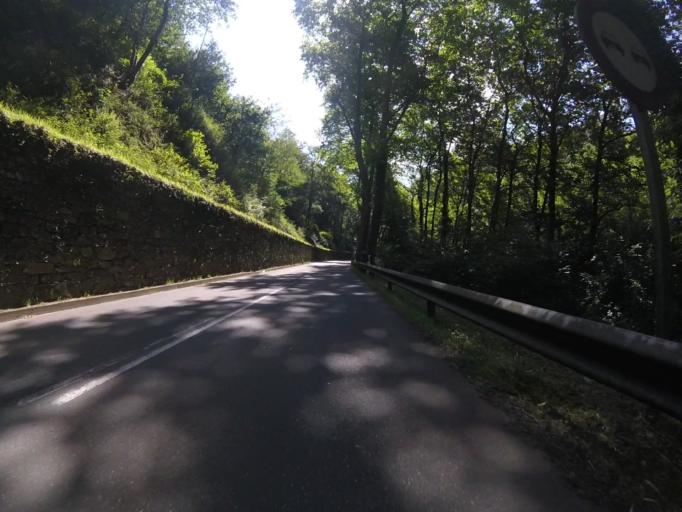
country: ES
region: Basque Country
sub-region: Provincia de Guipuzcoa
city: Azpeitia
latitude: 43.1794
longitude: -2.2425
